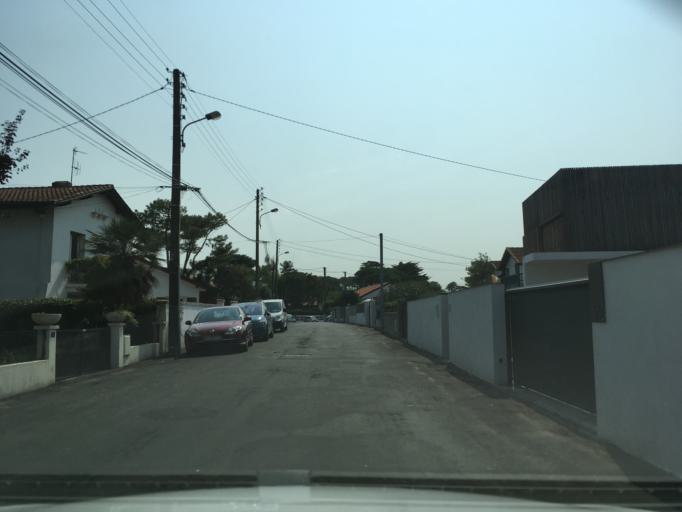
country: FR
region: Aquitaine
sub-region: Departement des Pyrenees-Atlantiques
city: Anglet
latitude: 43.5047
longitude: -1.5299
